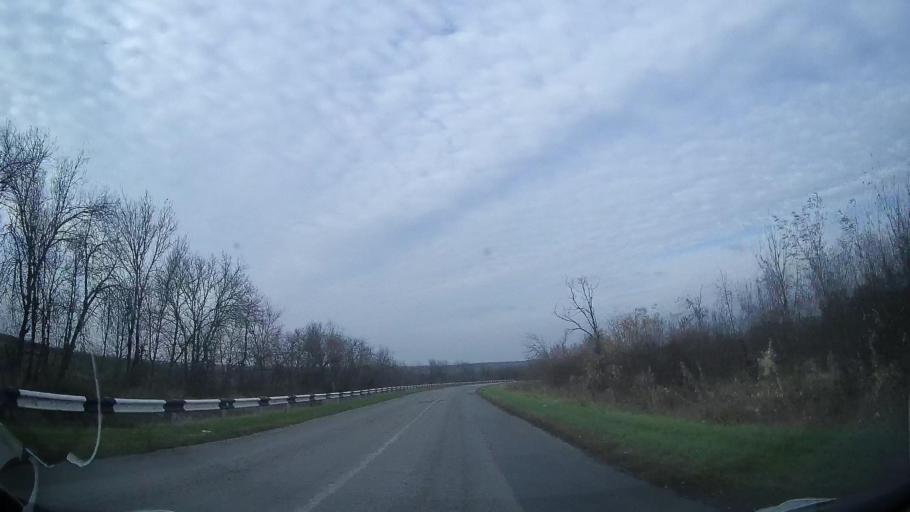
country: RU
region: Rostov
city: Zernograd
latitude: 46.8877
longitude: 40.3400
